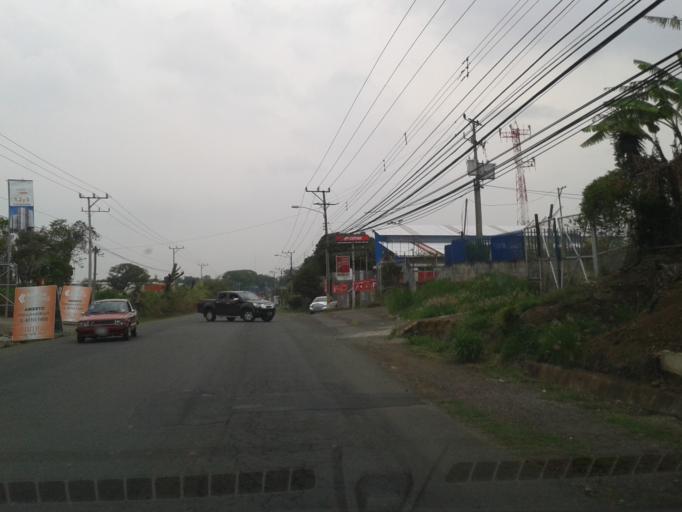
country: CR
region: Heredia
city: San Francisco
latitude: 9.9688
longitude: -84.1284
